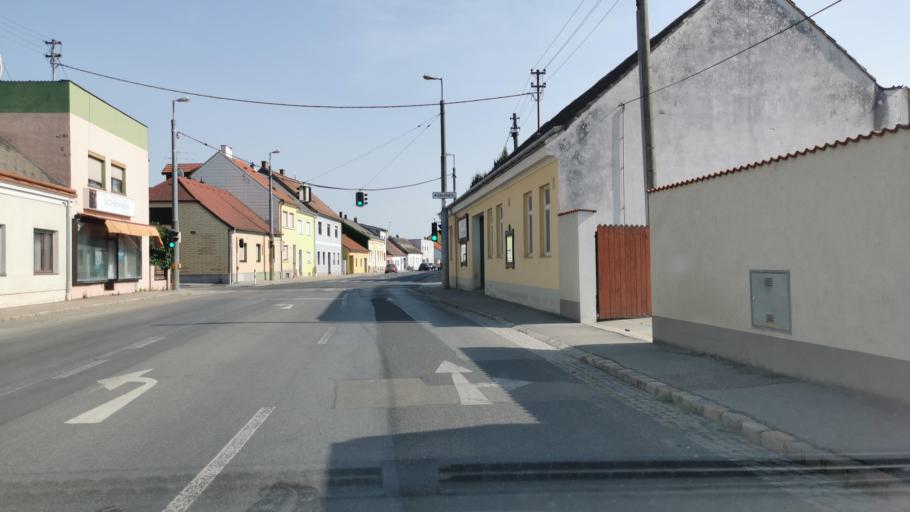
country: AT
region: Lower Austria
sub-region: Politischer Bezirk Mistelbach
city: Mistelbach
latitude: 48.5746
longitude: 16.5705
